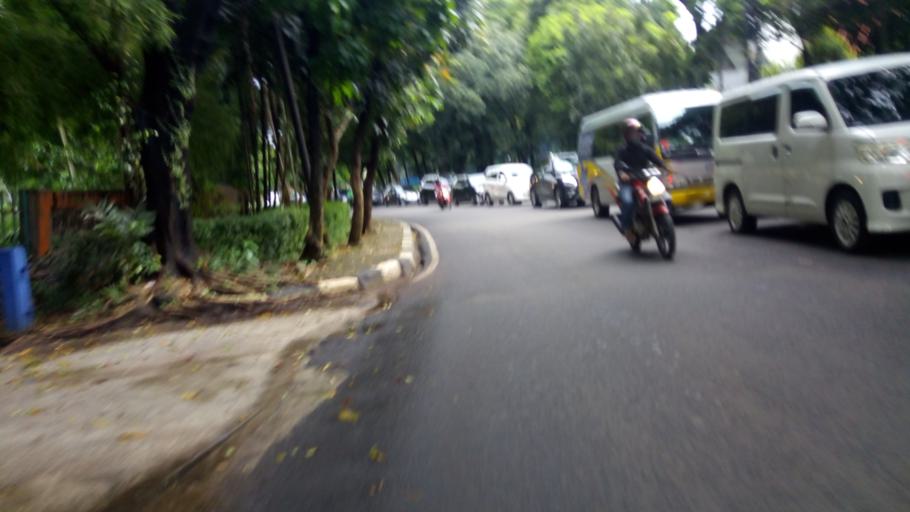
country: ID
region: Jakarta Raya
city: Jakarta
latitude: -6.2486
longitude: 106.8047
